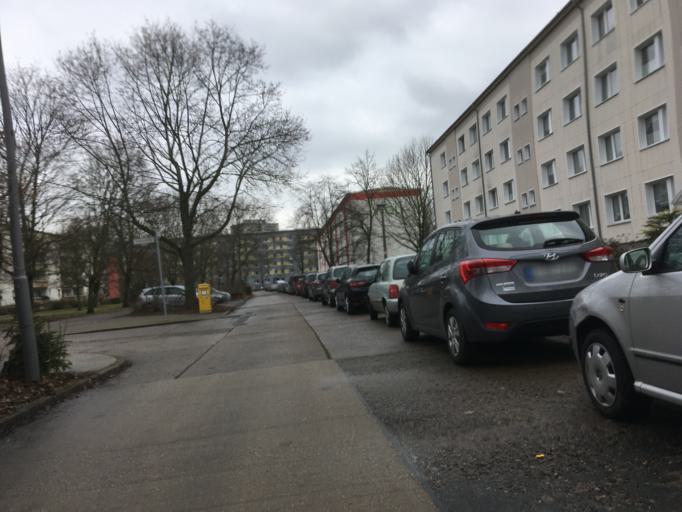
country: DE
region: Berlin
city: Friedrichsfelde
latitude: 52.4979
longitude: 13.5120
